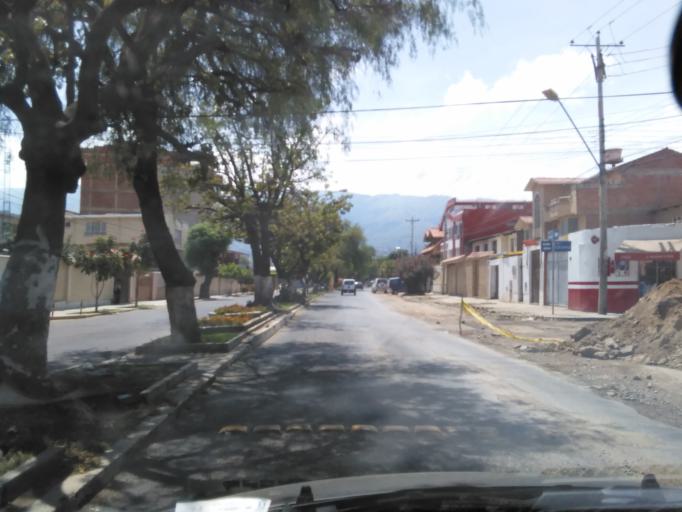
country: BO
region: Cochabamba
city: Cochabamba
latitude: -17.3853
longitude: -66.1651
